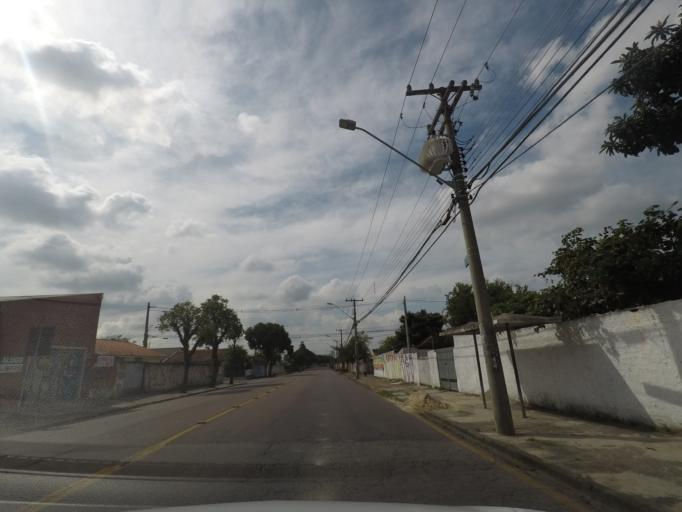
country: BR
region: Parana
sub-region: Pinhais
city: Pinhais
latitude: -25.4754
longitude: -49.2015
